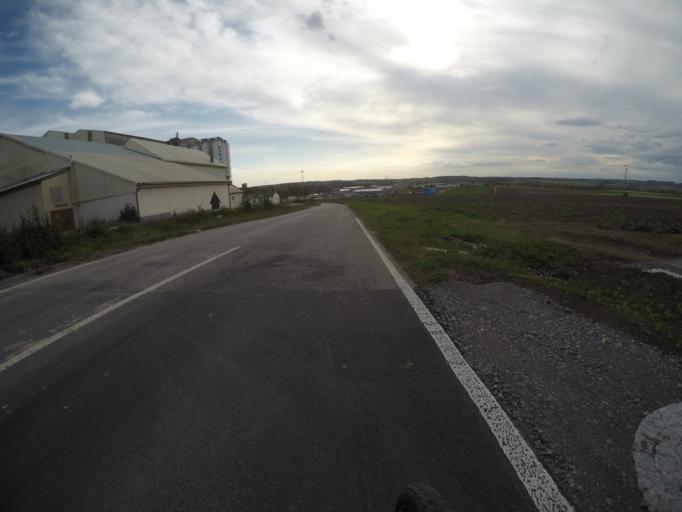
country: DE
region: Baden-Wuerttemberg
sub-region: Regierungsbezirk Stuttgart
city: Herrenberg
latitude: 48.5718
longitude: 8.9132
